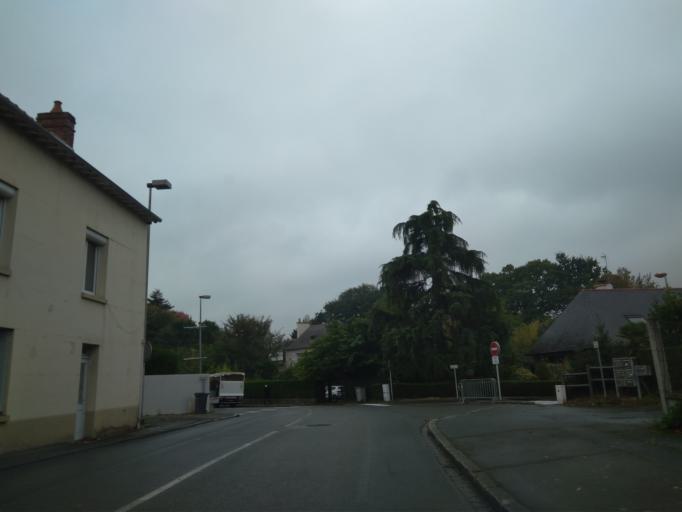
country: FR
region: Brittany
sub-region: Departement d'Ille-et-Vilaine
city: Saint-Gregoire
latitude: 48.1509
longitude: -1.6821
